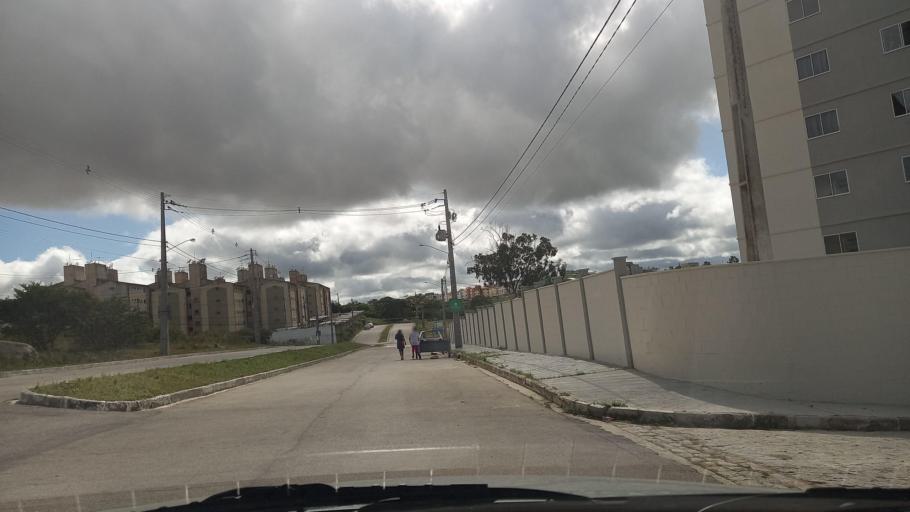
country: BR
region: Pernambuco
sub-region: Caruaru
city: Caruaru
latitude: -8.3037
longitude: -35.9599
